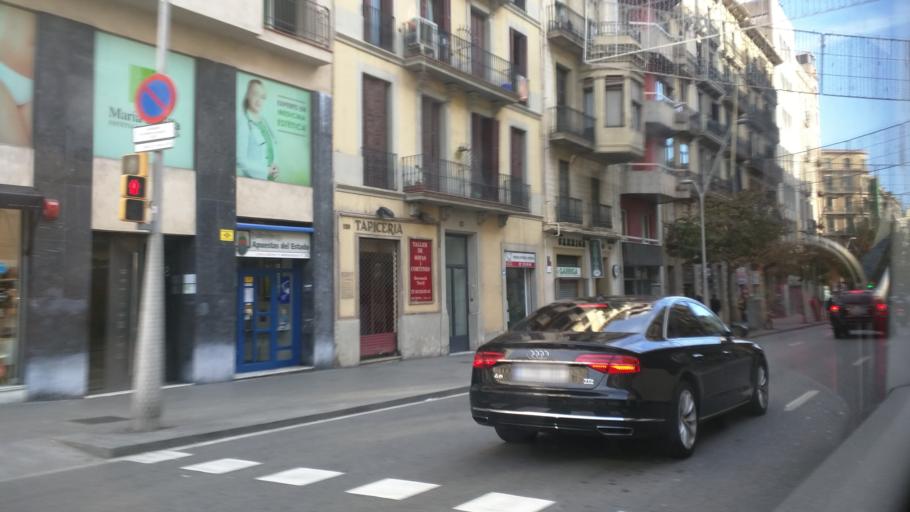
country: ES
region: Catalonia
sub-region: Provincia de Barcelona
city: Barcelona
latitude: 41.3933
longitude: 2.1576
